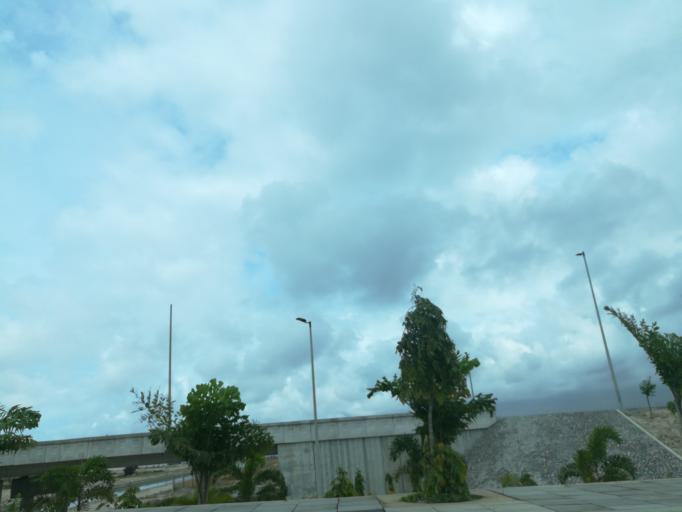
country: NG
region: Lagos
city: Lagos
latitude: 6.4135
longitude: 3.4113
